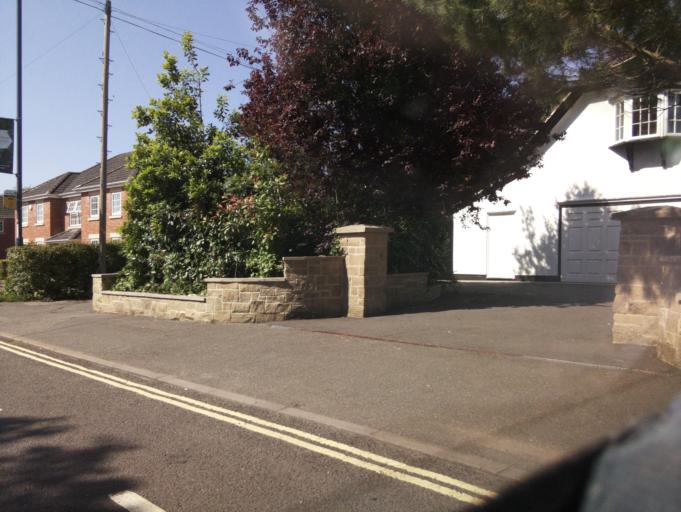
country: GB
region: England
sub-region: Derby
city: Derby
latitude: 52.9437
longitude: -1.4842
